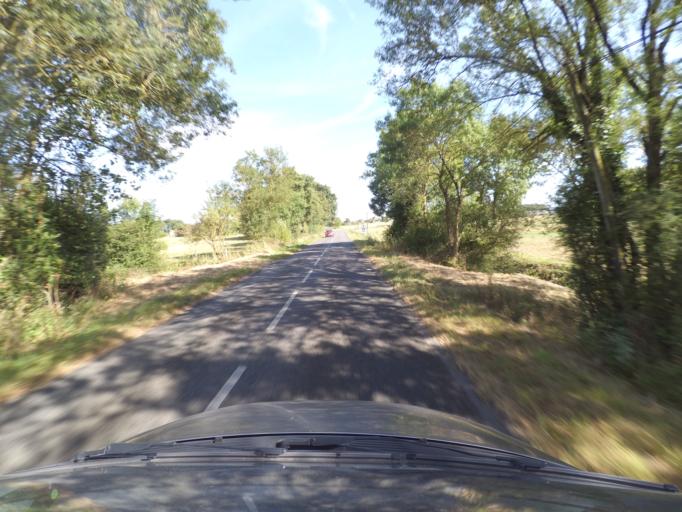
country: FR
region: Pays de la Loire
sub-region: Departement de la Loire-Atlantique
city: Le Bignon
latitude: 47.1145
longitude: -1.5197
